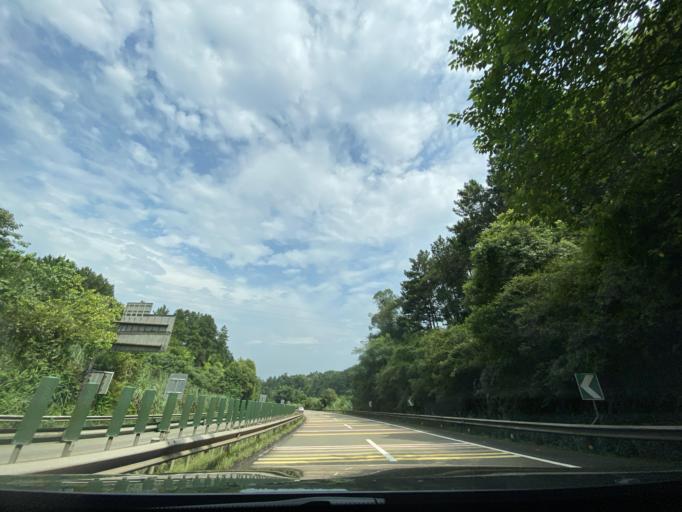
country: CN
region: Sichuan
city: Chonglong
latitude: 29.8003
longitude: 104.7115
